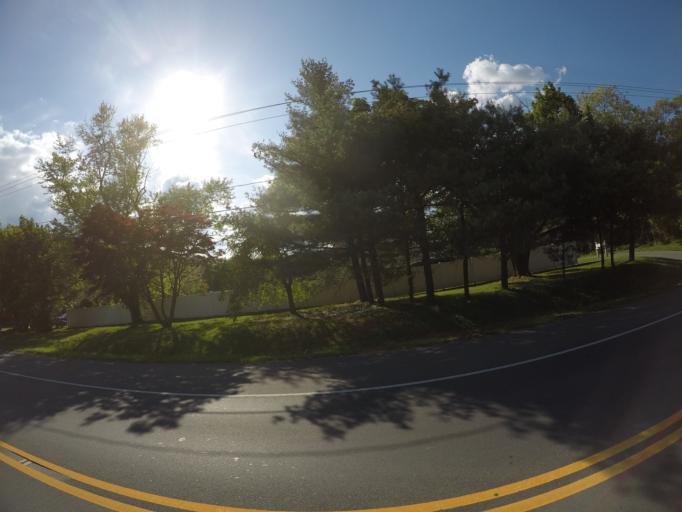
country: US
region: Maryland
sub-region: Montgomery County
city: Damascus
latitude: 39.2566
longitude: -77.2230
